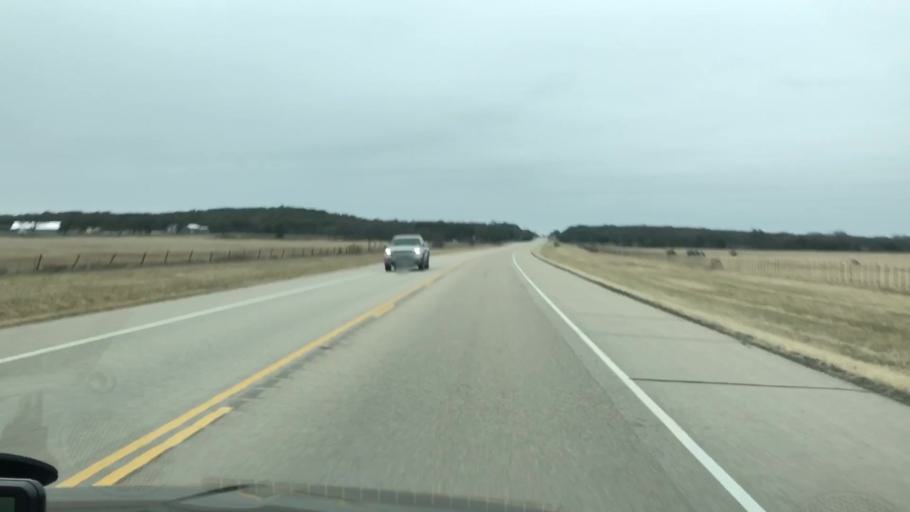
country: US
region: Texas
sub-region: Hamilton County
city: Hamilton
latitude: 31.7944
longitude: -98.1200
